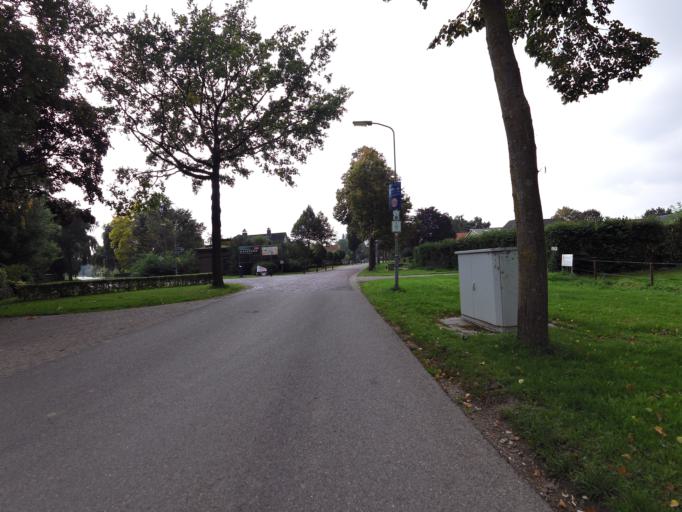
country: NL
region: Gelderland
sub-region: Gemeente Duiven
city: Duiven
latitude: 51.9315
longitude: 5.9951
